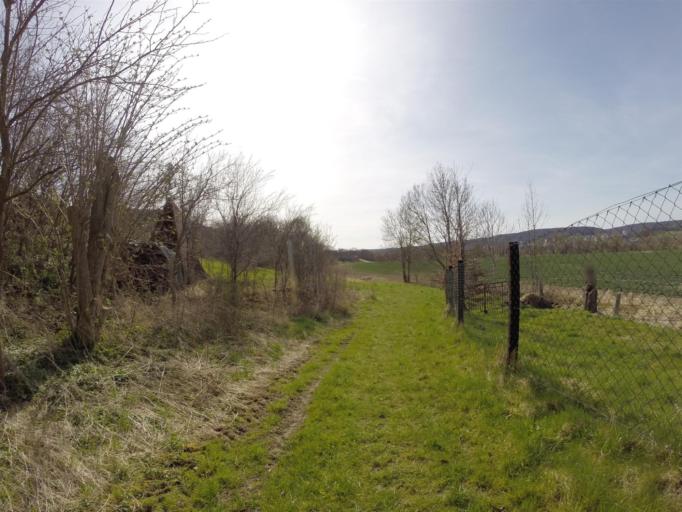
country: DE
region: Thuringia
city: Neuengonna
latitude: 50.9507
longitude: 11.6320
